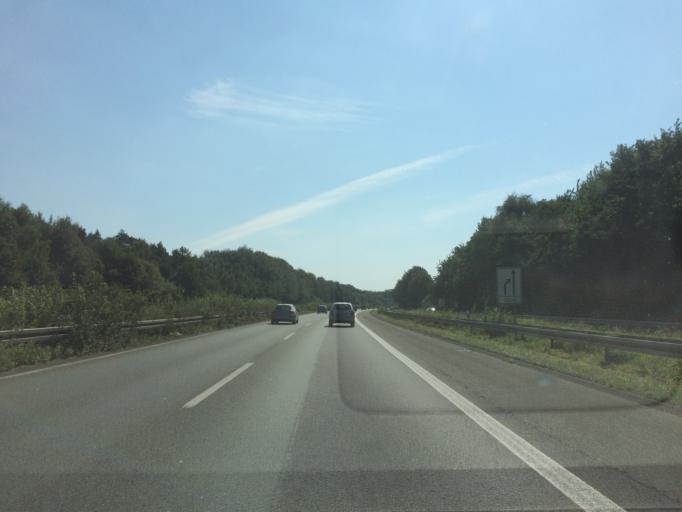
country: DE
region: North Rhine-Westphalia
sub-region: Regierungsbezirk Munster
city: Recklinghausen
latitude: 51.6537
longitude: 7.1682
